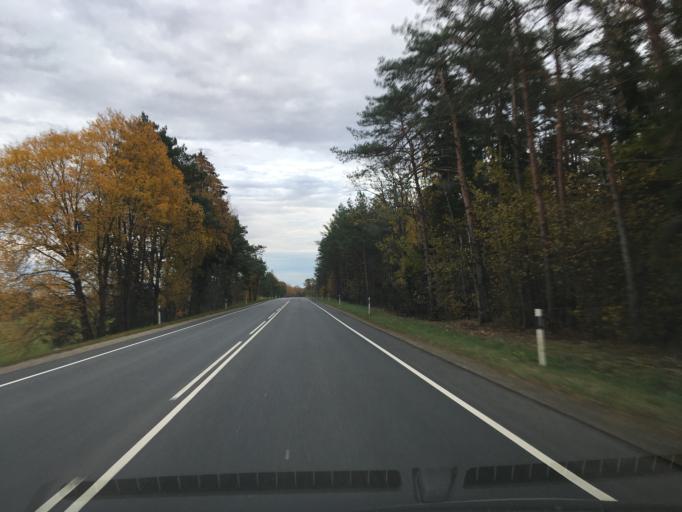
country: EE
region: Harju
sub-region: Nissi vald
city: Turba
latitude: 58.9986
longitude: 24.0898
